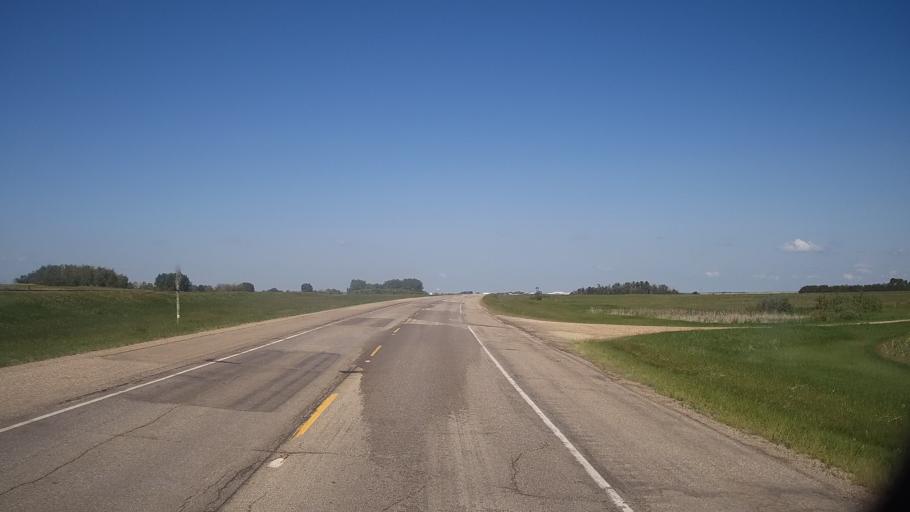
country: CA
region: Saskatchewan
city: Saskatoon
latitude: 51.9951
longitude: -106.0989
